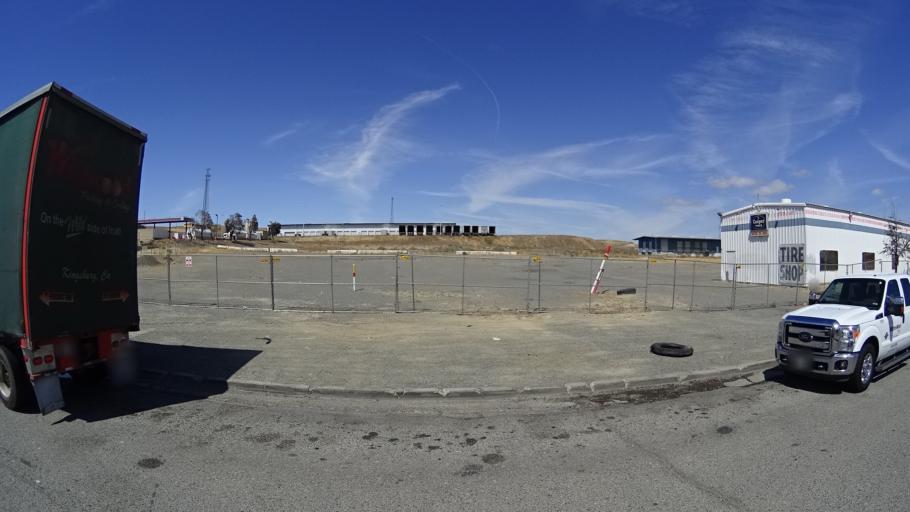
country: US
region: California
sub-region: Kings County
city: Kettleman City
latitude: 35.9890
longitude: -119.9605
